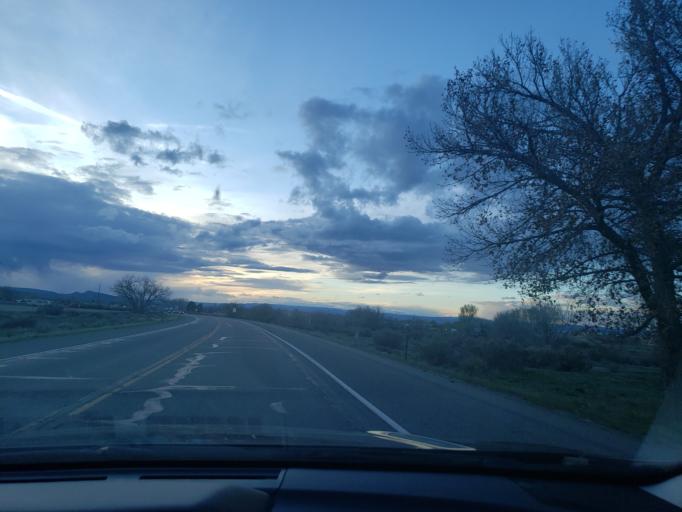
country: US
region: Colorado
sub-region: Mesa County
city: Fruita
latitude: 39.1445
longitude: -108.7107
